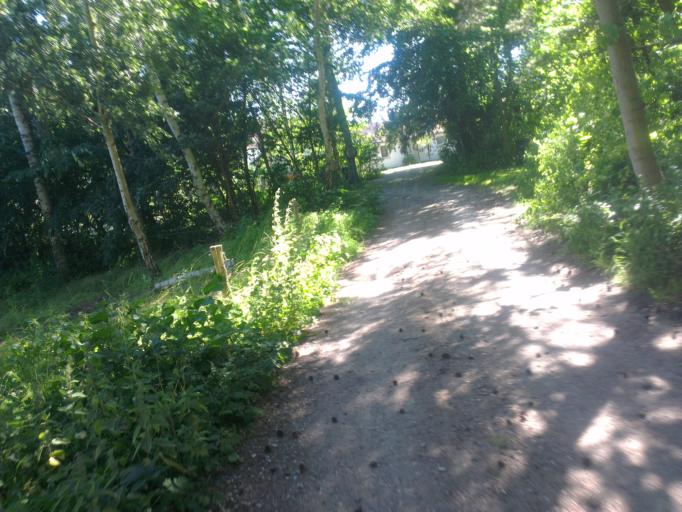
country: DK
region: Capital Region
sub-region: Frederikssund Kommune
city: Jaegerspris
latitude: 55.9081
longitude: 11.9172
